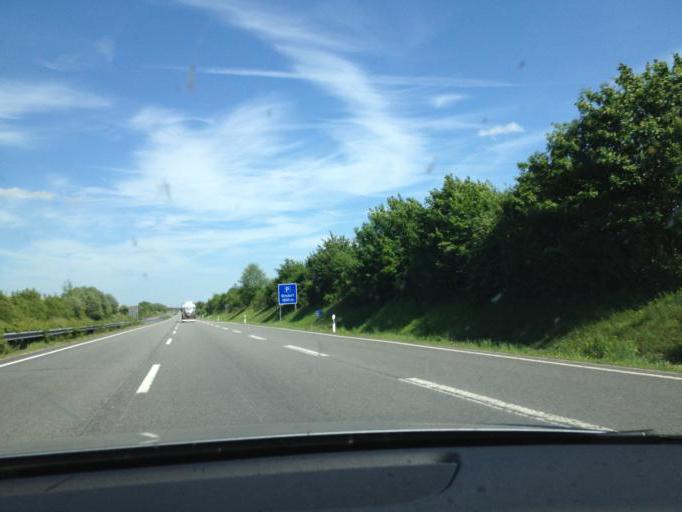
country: DE
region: Rheinland-Pfalz
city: Orsfeld
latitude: 50.0182
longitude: 6.6146
